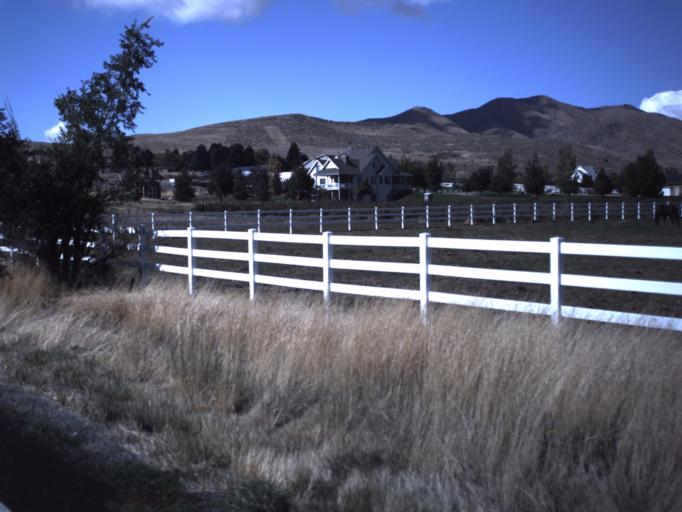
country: US
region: Utah
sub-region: Utah County
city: West Mountain
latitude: 40.0191
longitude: -111.7900
